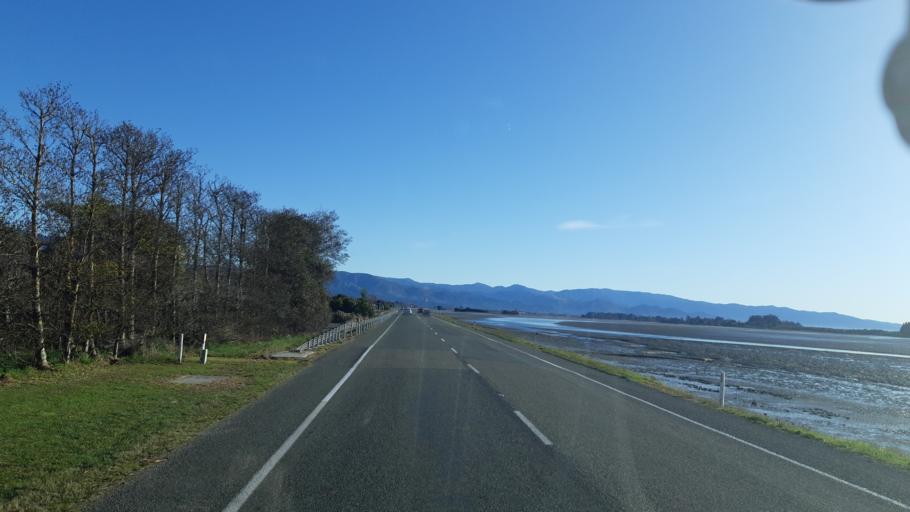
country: NZ
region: Tasman
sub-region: Tasman District
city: Motueka
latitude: -41.1796
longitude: 173.0439
